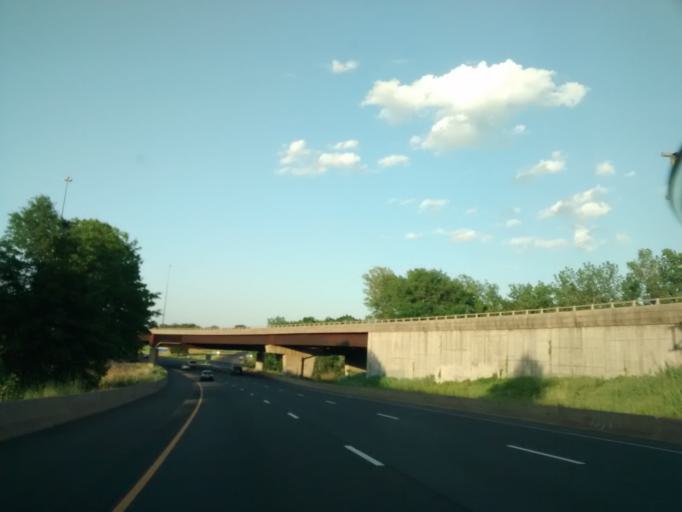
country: US
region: Connecticut
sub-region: Hartford County
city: East Hartford
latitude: 41.7634
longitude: -72.6323
